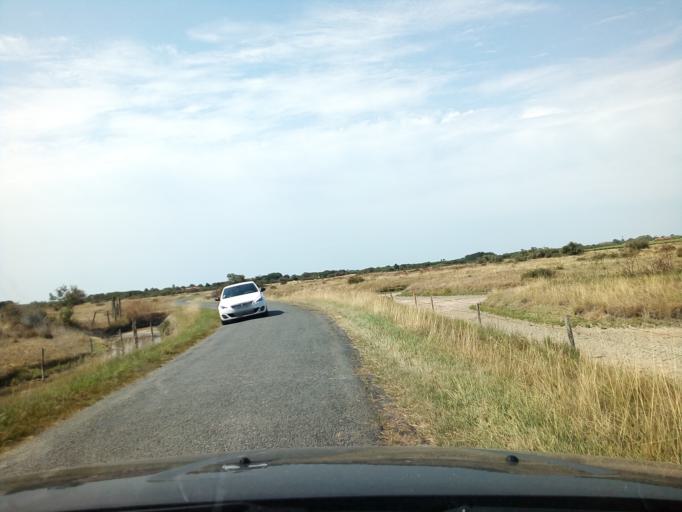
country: FR
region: Poitou-Charentes
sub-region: Departement de la Charente-Maritime
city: Dolus-d'Oleron
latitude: 45.9507
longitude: -1.2854
